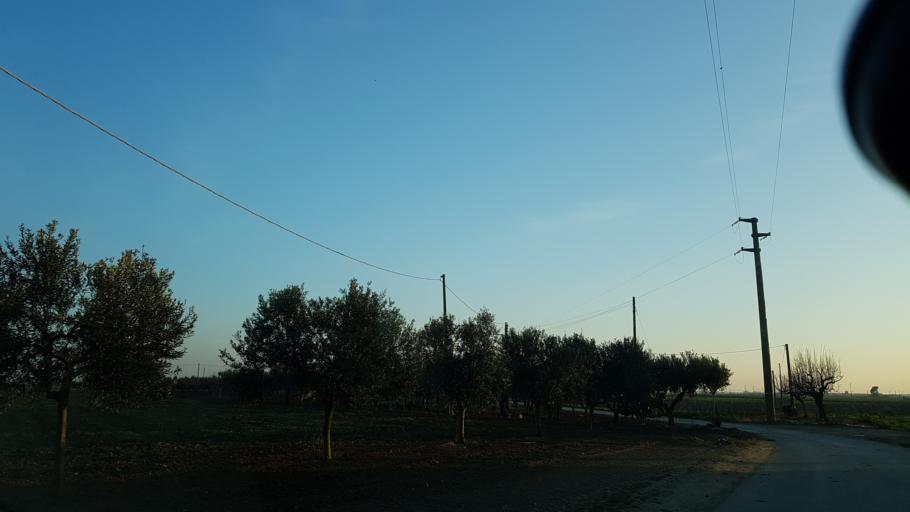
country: IT
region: Apulia
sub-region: Provincia di Brindisi
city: La Rosa
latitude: 40.5925
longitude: 17.9351
